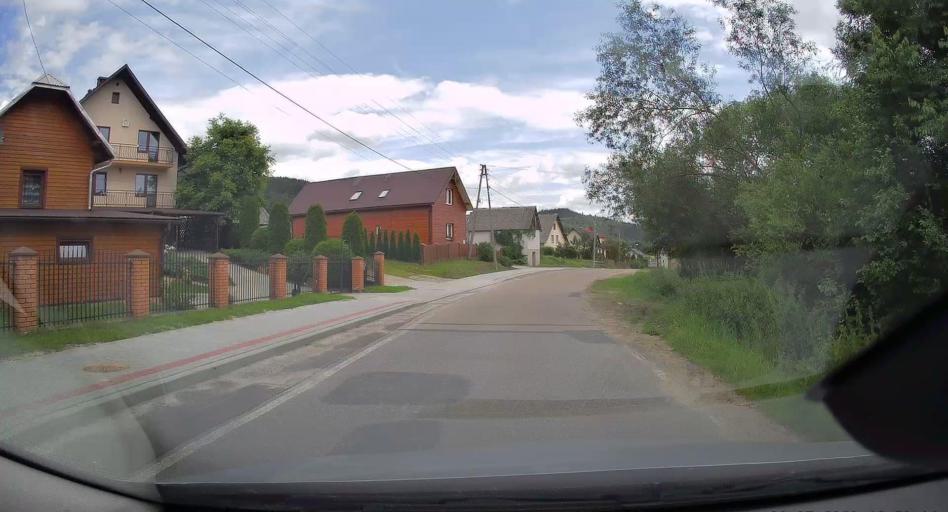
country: PL
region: Lesser Poland Voivodeship
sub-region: Powiat nowosadecki
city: Muszyna
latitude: 49.3896
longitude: 20.9088
